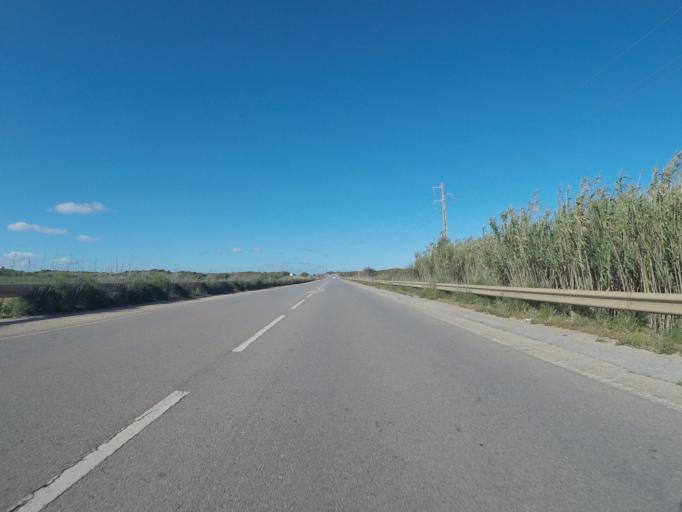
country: PT
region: Faro
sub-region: Vila do Bispo
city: Vila do Bispo
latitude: 37.0495
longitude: -8.9278
